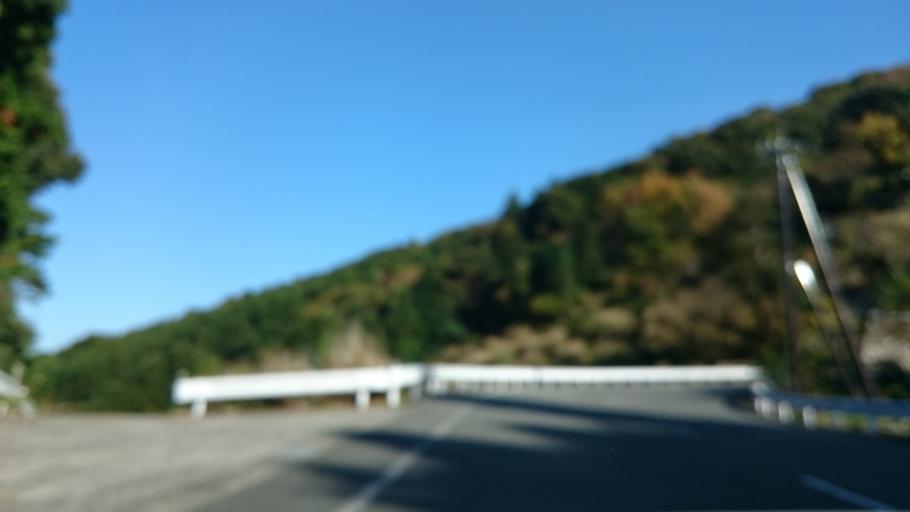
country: JP
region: Shizuoka
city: Heda
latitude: 35.0044
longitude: 138.8313
